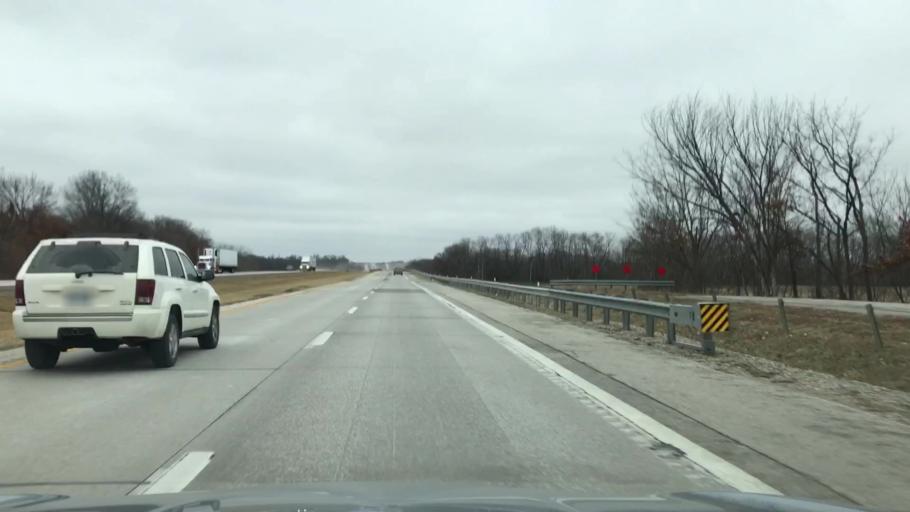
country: US
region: Missouri
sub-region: Linn County
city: Marceline
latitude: 39.7615
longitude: -92.9871
